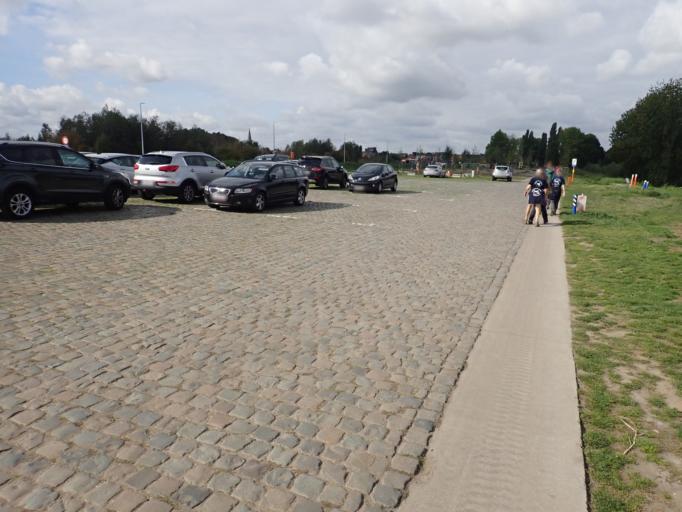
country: BE
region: Flanders
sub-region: Provincie Oost-Vlaanderen
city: Kruibeke
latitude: 51.1756
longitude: 4.3232
